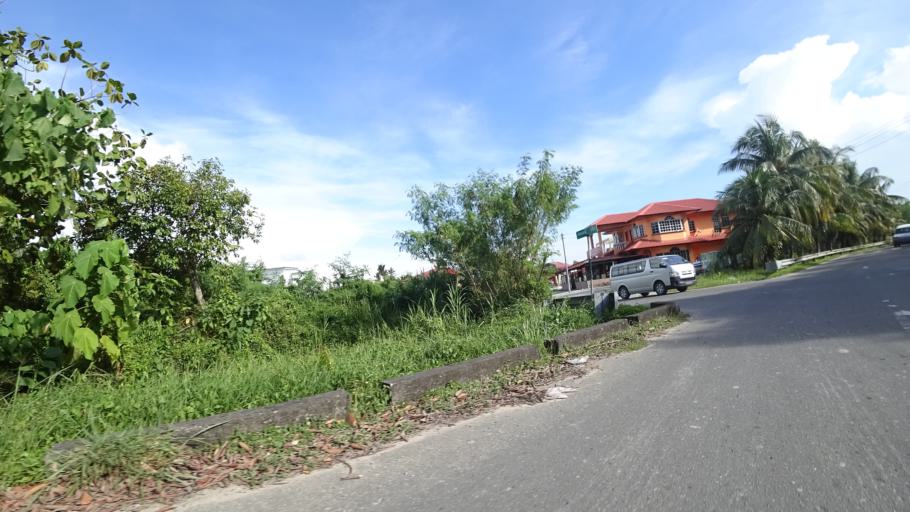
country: BN
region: Brunei and Muara
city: Bandar Seri Begawan
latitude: 4.8946
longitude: 114.8452
